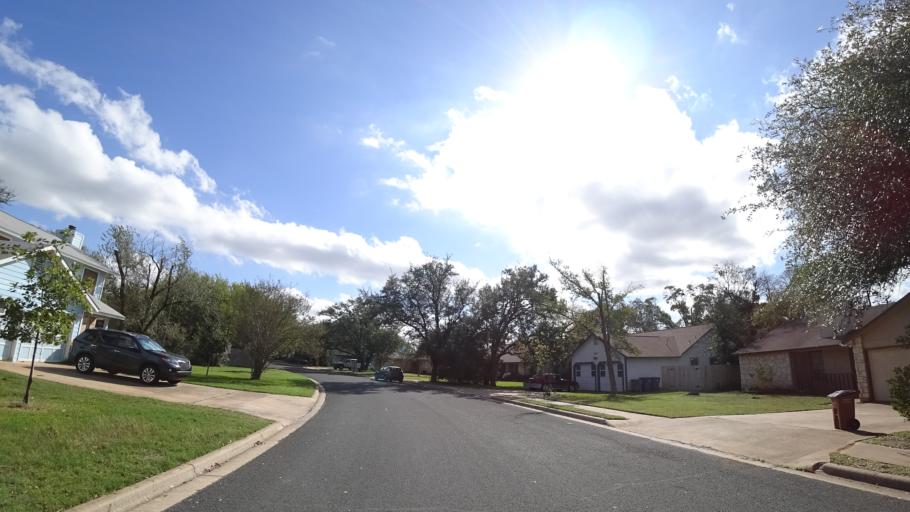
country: US
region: Texas
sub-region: Williamson County
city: Jollyville
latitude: 30.4230
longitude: -97.7292
